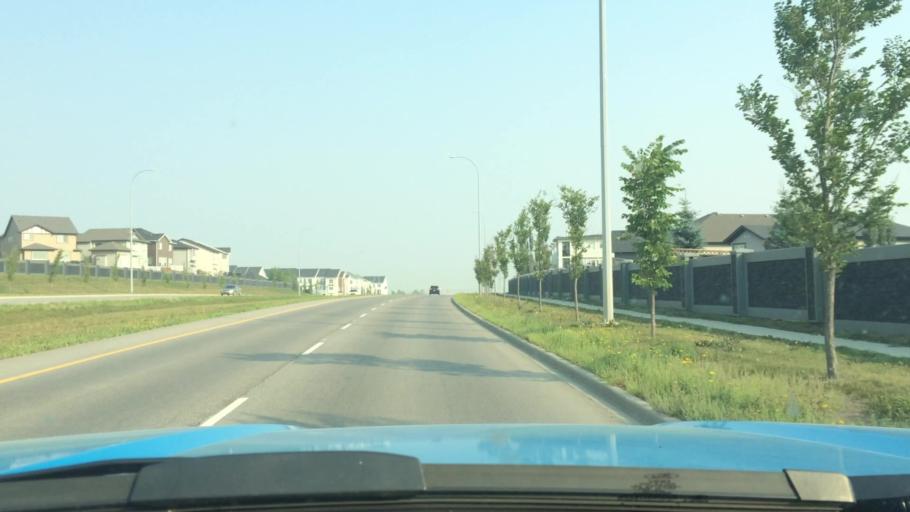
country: CA
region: Alberta
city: Calgary
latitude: 51.1777
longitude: -114.1583
